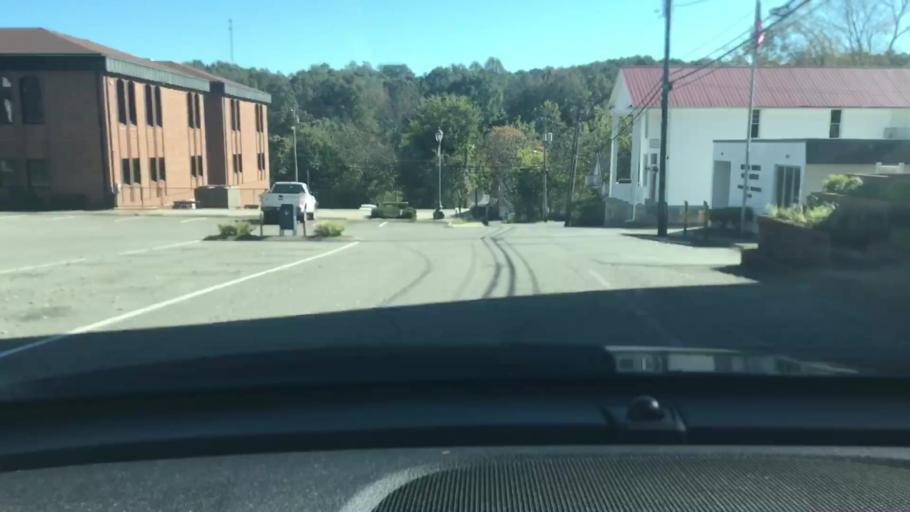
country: US
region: Tennessee
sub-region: Dickson County
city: Charlotte
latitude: 36.1782
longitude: -87.3401
